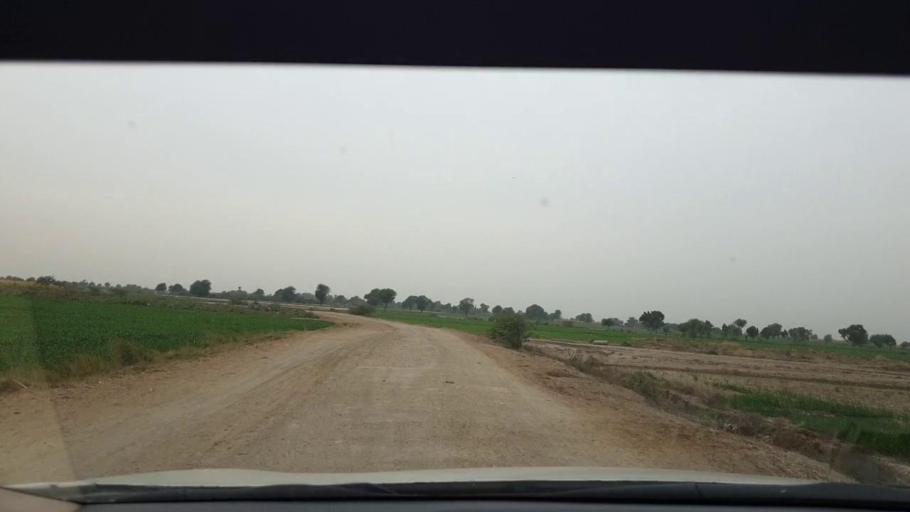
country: PK
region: Sindh
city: Berani
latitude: 25.8842
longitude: 68.8017
